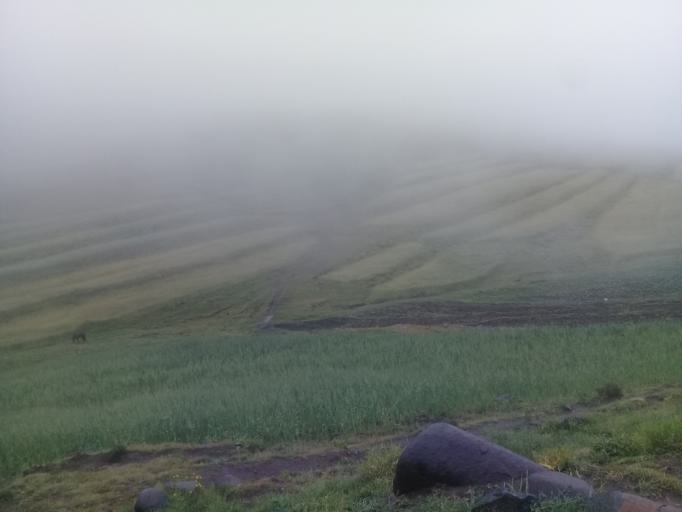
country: LS
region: Mokhotlong
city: Mokhotlong
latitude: -29.3876
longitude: 28.9748
